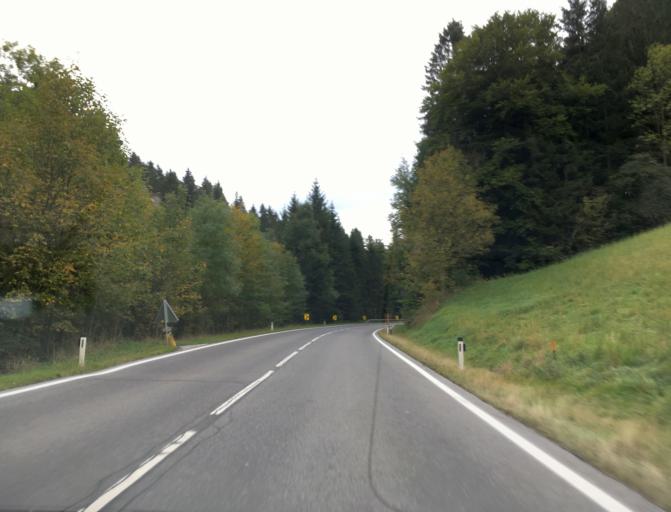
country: AT
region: Lower Austria
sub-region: Politischer Bezirk Neunkirchen
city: Thomasberg
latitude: 47.5588
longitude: 16.1432
